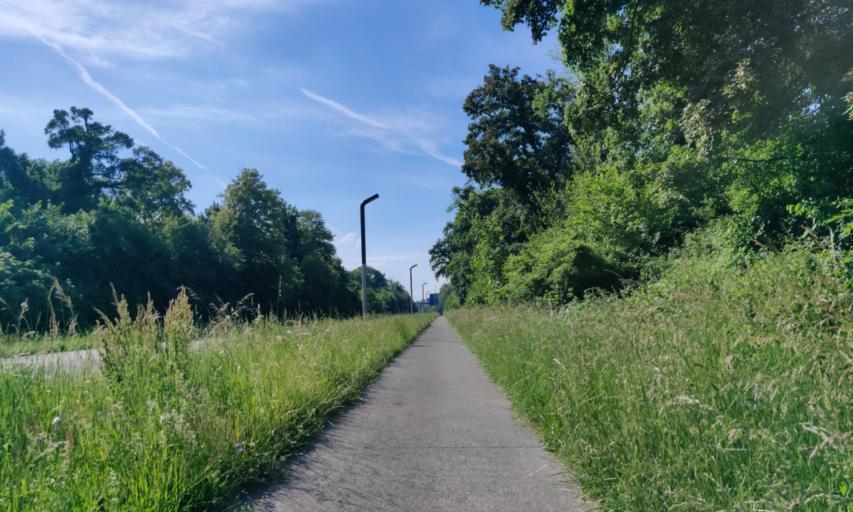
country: CH
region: Basel-Landschaft
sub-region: Bezirk Arlesheim
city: Muttenz
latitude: 47.5402
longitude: 7.6546
